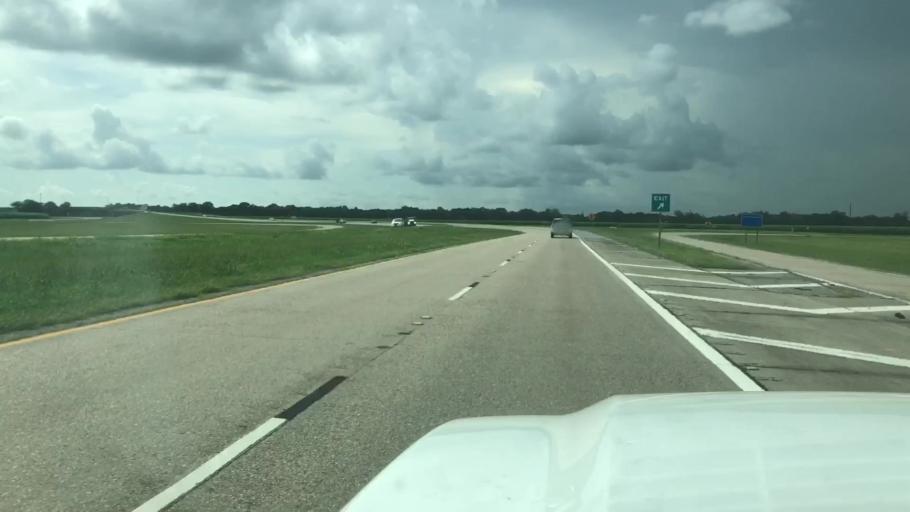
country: US
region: Louisiana
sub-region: Saint Mary Parish
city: Franklin
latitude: 29.7568
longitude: -91.4555
